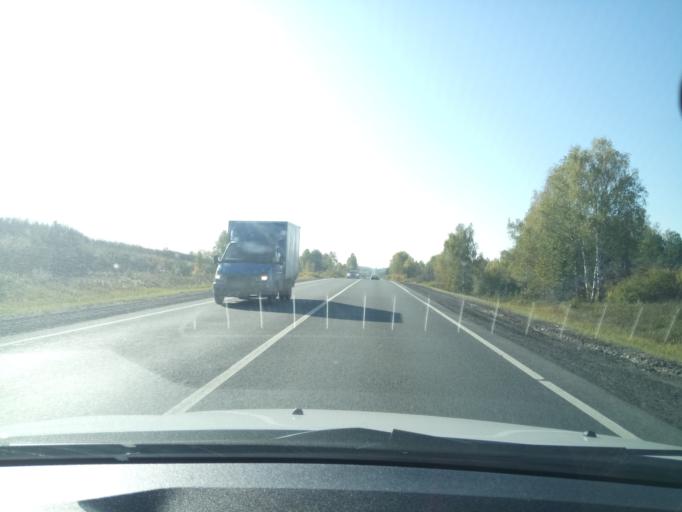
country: RU
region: Nizjnij Novgorod
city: Dal'neye Konstantinovo
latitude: 55.9713
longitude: 43.9734
